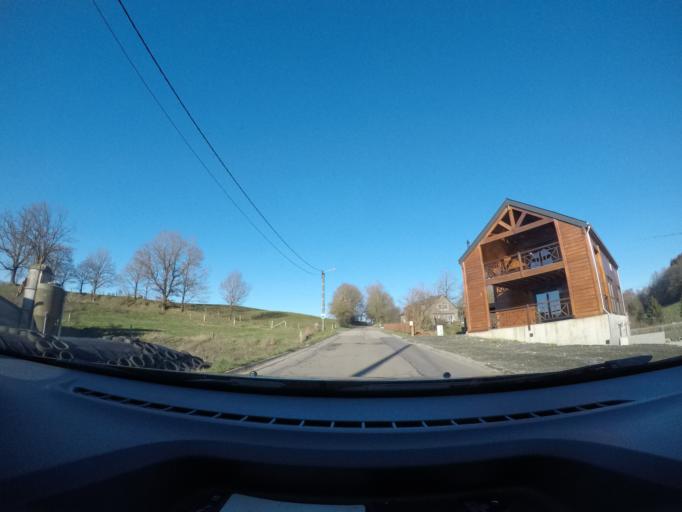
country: BE
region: Wallonia
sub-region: Province du Luxembourg
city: Bertrix
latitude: 49.8384
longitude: 5.2985
